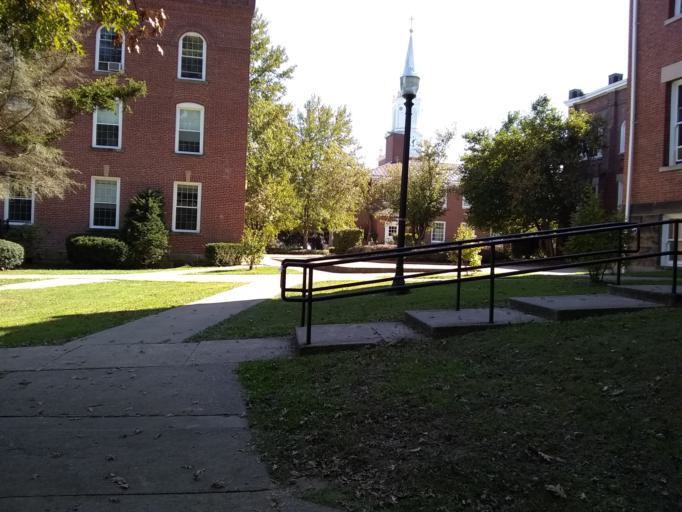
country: US
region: West Virginia
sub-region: Upshur County
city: Buckhannon
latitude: 38.9903
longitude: -80.2196
